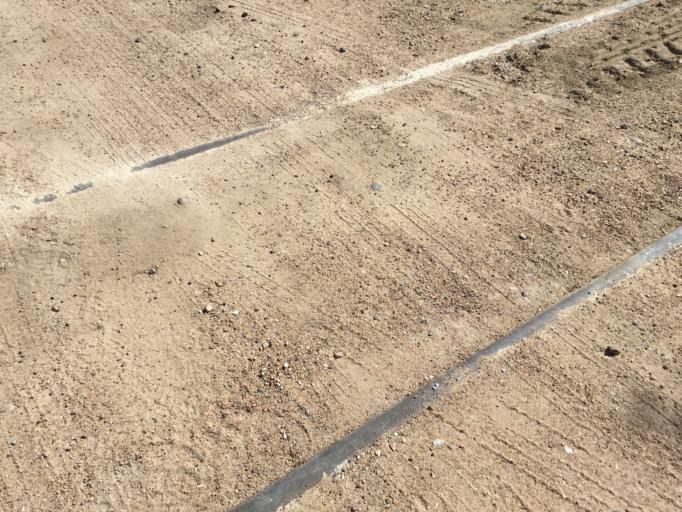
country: US
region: Kansas
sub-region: Pratt County
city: Pratt
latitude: 37.5101
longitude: -98.8232
